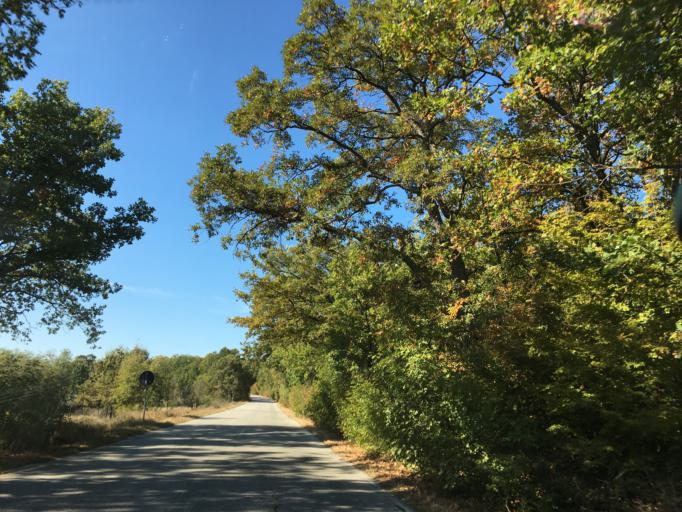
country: BG
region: Khaskovo
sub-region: Obshtina Ivaylovgrad
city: Ivaylovgrad
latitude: 41.5206
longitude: 26.0281
